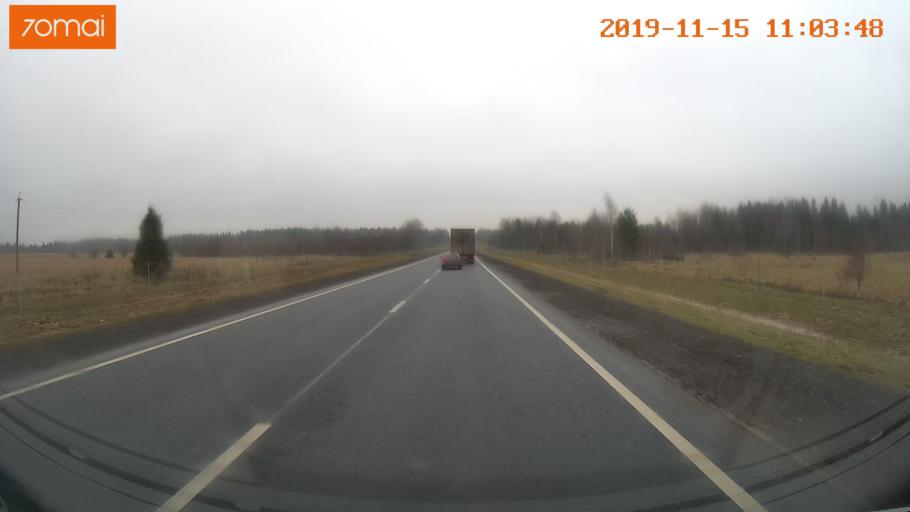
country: RU
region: Vologda
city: Chebsara
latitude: 59.1229
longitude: 38.9702
